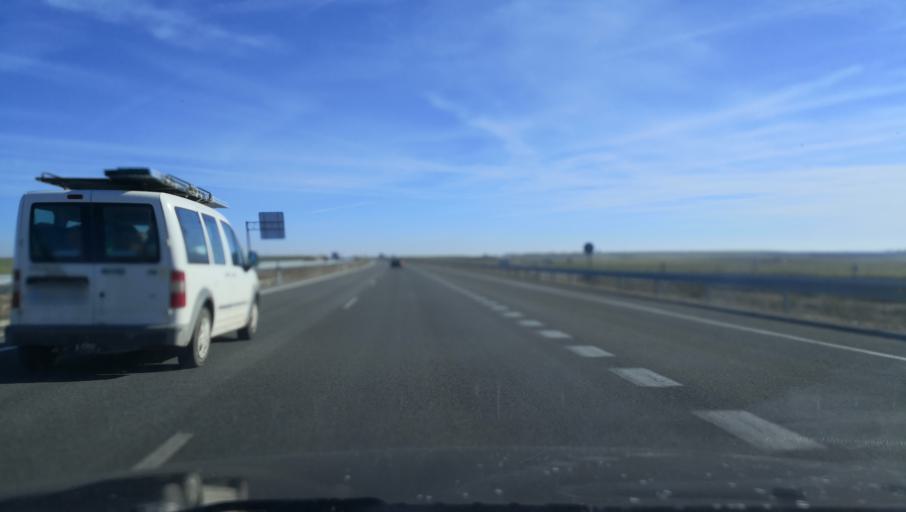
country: ES
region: Castille and Leon
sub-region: Provincia de Salamanca
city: Alconada
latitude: 40.9293
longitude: -5.3768
